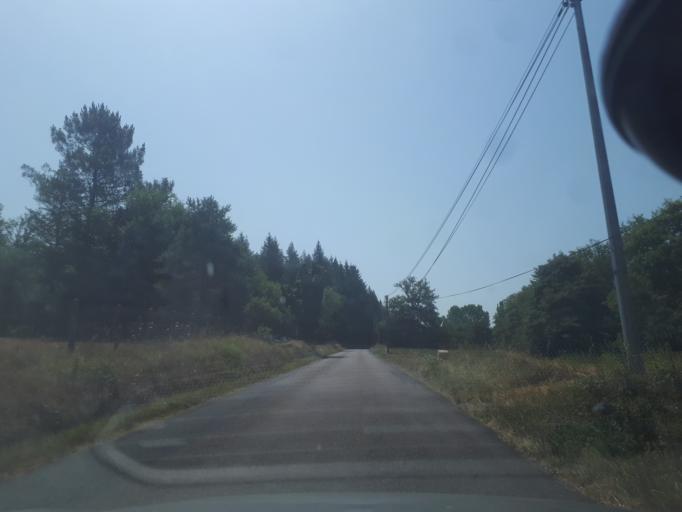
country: FR
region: Midi-Pyrenees
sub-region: Departement du Lot
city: Gourdon
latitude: 44.7809
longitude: 1.3651
